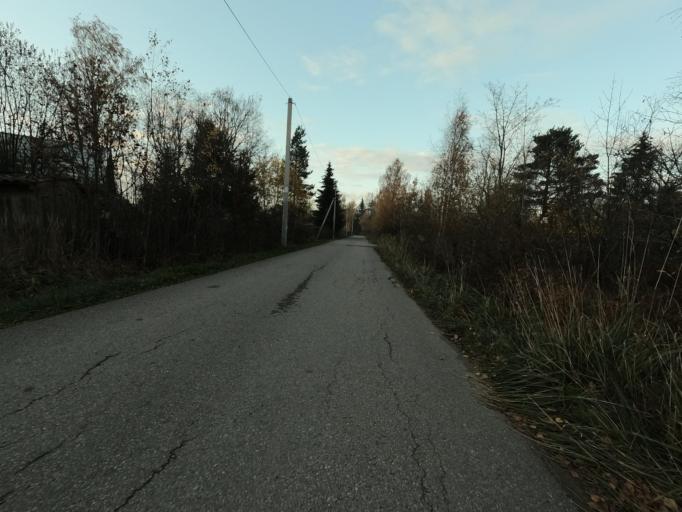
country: RU
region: Leningrad
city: Mga
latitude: 59.7791
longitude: 31.2046
